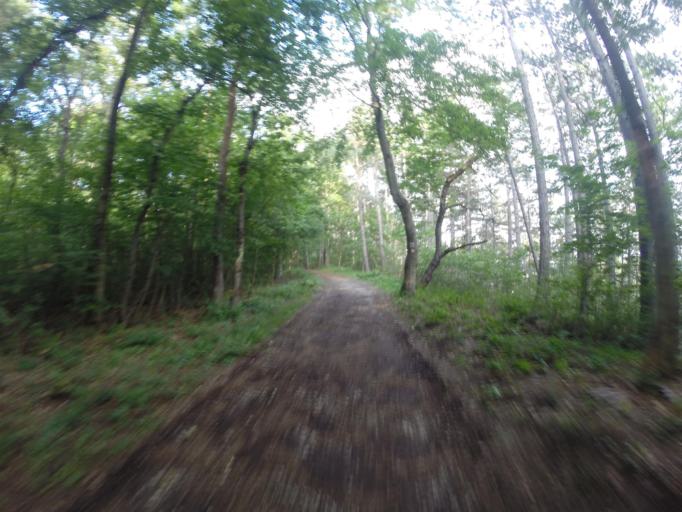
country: DE
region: Thuringia
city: Grosslobichau
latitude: 50.9388
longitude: 11.6549
